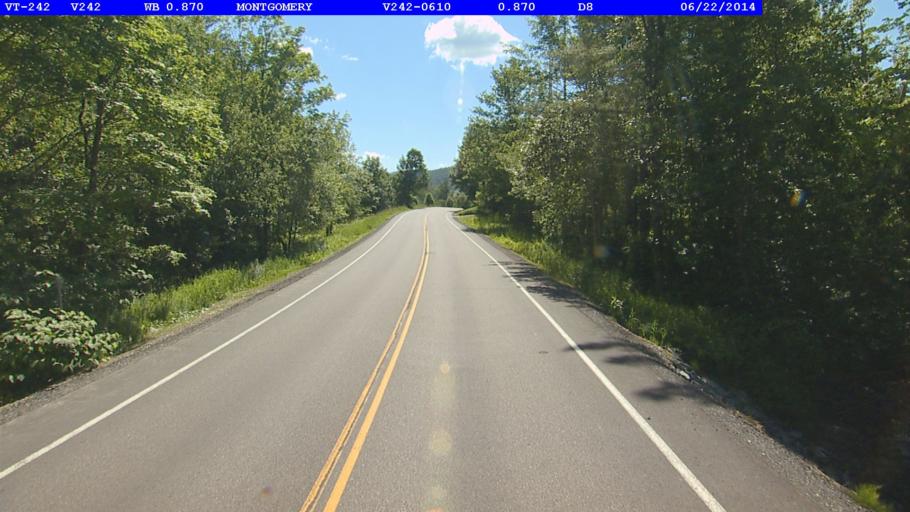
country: US
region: Vermont
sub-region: Franklin County
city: Richford
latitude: 44.8830
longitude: -72.5949
